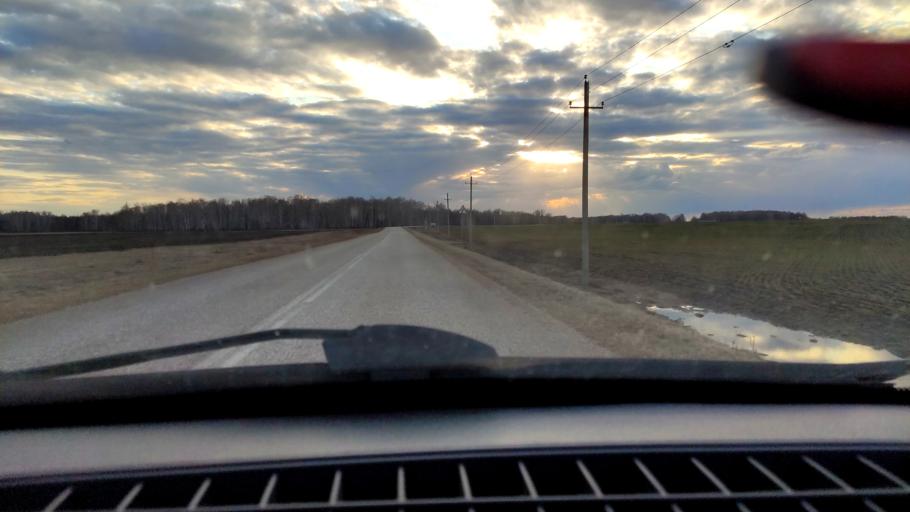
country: RU
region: Bashkortostan
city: Tolbazy
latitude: 54.0039
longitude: 55.6214
